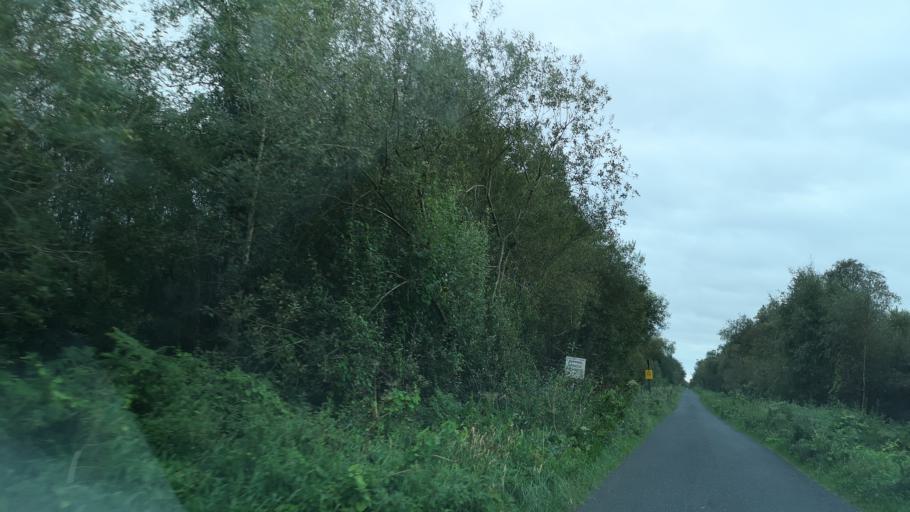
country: IE
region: Leinster
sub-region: Uibh Fhaili
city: Ferbane
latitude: 53.1995
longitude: -7.7252
